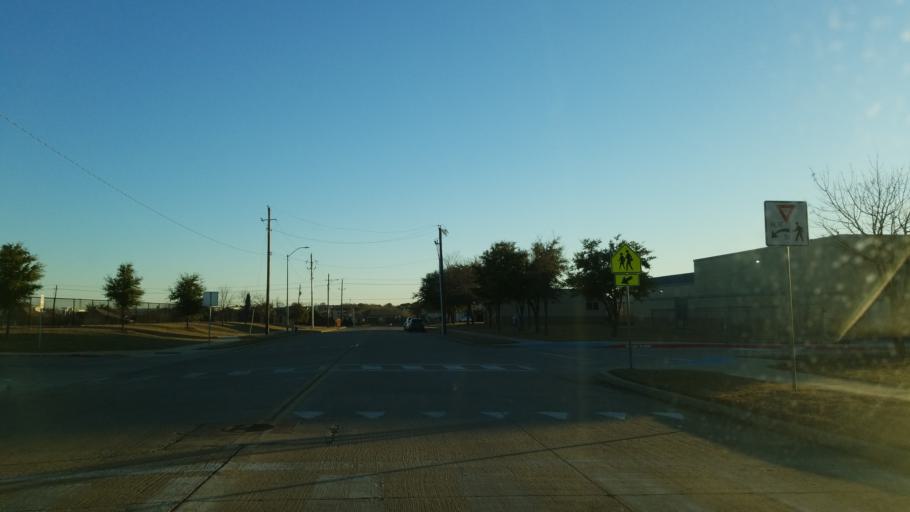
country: US
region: Texas
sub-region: Tarrant County
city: Arlington
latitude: 32.7295
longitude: -97.0540
